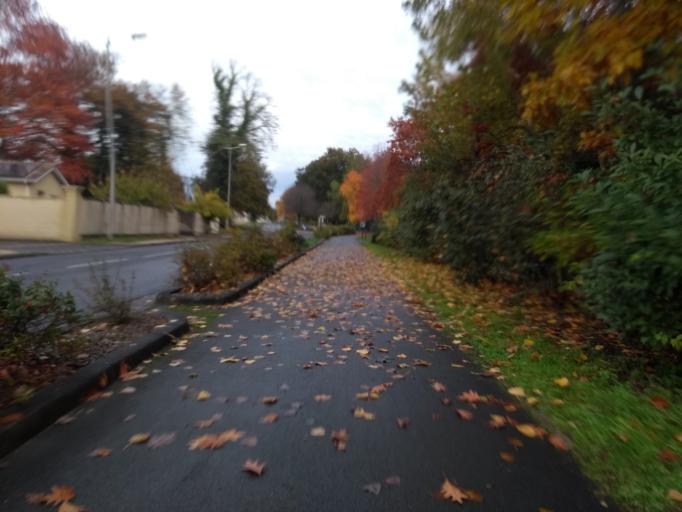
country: FR
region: Aquitaine
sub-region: Departement de la Gironde
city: Canejan
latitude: 44.7672
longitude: -0.6346
